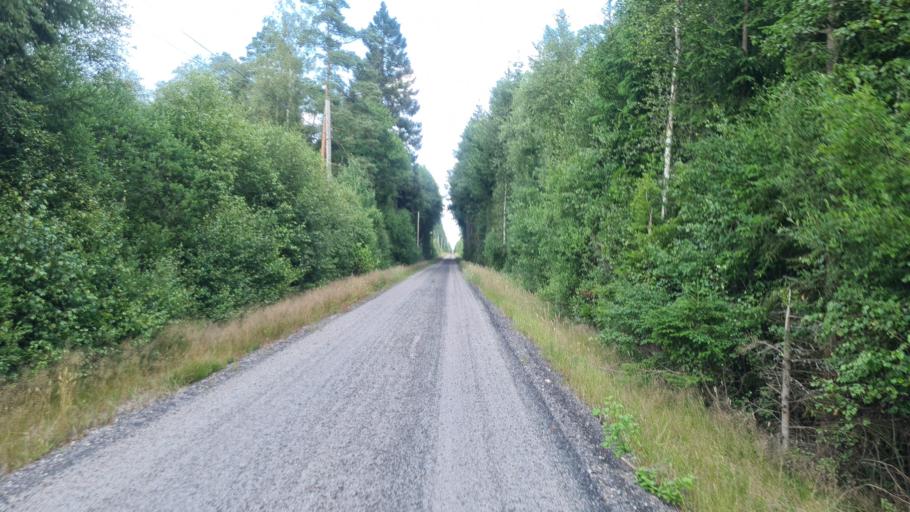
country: SE
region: Kronoberg
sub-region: Ljungby Kommun
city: Lagan
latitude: 56.8575
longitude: 14.1280
